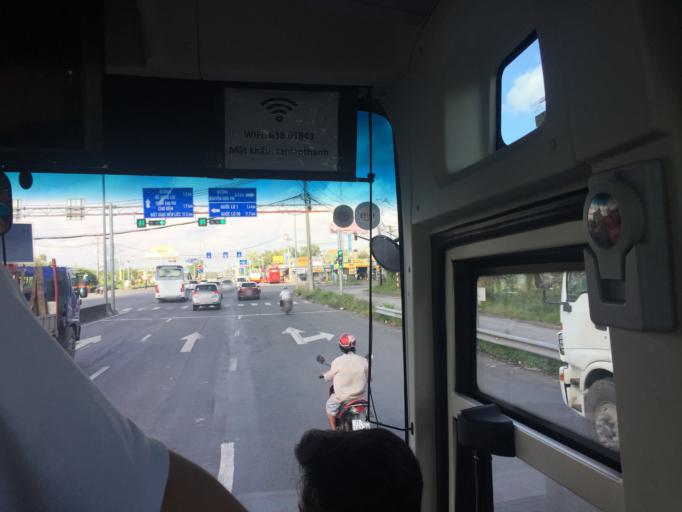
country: VN
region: Ho Chi Minh City
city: Tan Tuc
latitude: 10.6865
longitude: 106.5769
